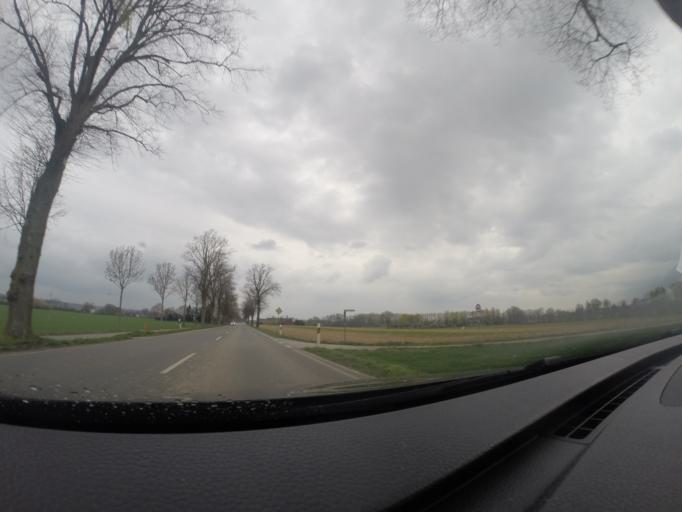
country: DE
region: North Rhine-Westphalia
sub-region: Regierungsbezirk Dusseldorf
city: Xanten
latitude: 51.6768
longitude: 6.4225
